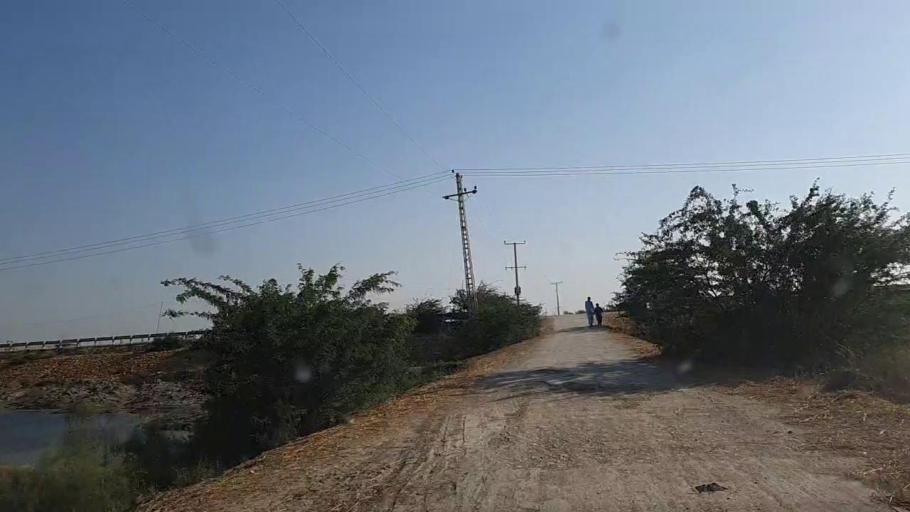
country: PK
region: Sindh
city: Thatta
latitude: 24.6191
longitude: 68.0780
